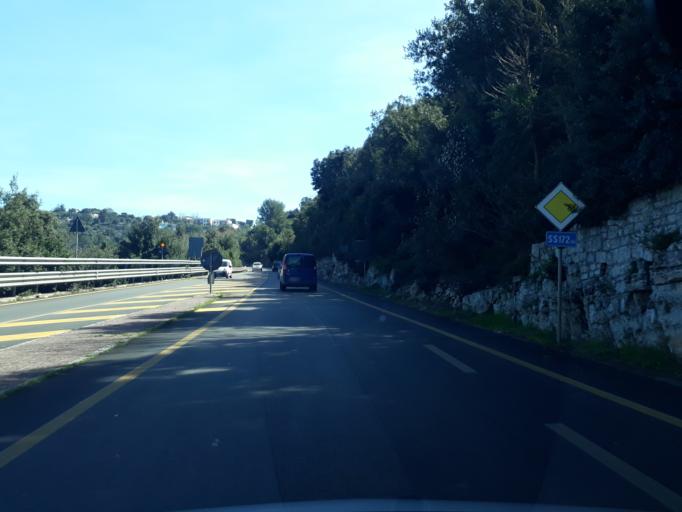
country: IT
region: Apulia
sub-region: Provincia di Brindisi
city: Lamie di Olimpie-Selva
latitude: 40.8061
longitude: 17.3479
